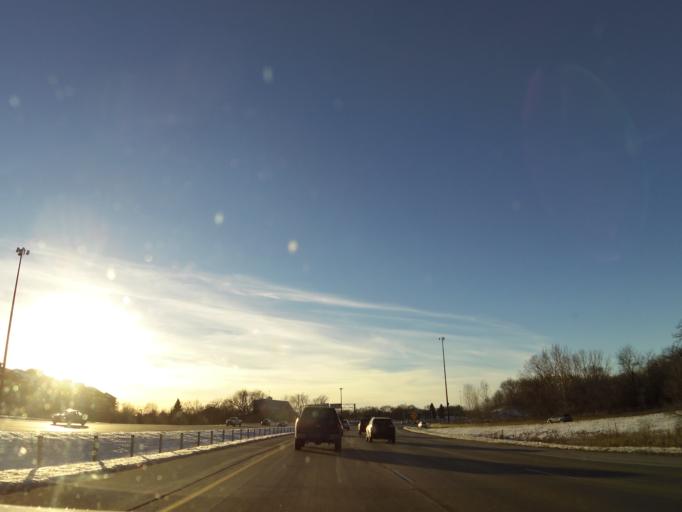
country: US
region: Minnesota
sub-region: Hennepin County
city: Eden Prairie
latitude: 44.8612
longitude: -93.4460
